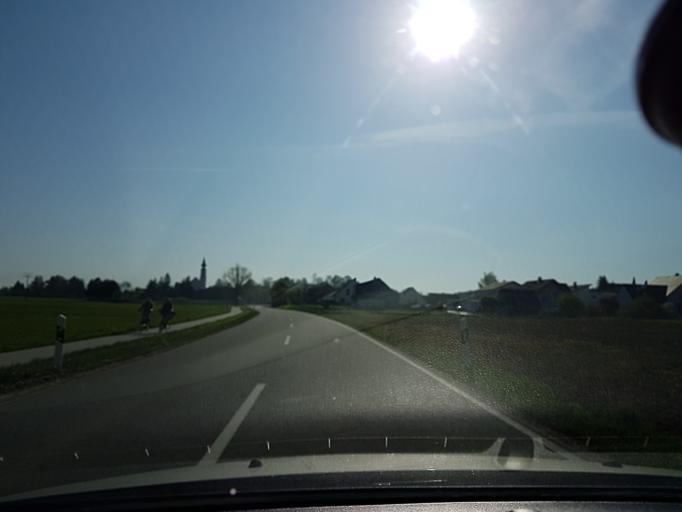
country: DE
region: Bavaria
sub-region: Lower Bavaria
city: Altfraunhofen
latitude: 48.4481
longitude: 12.1597
